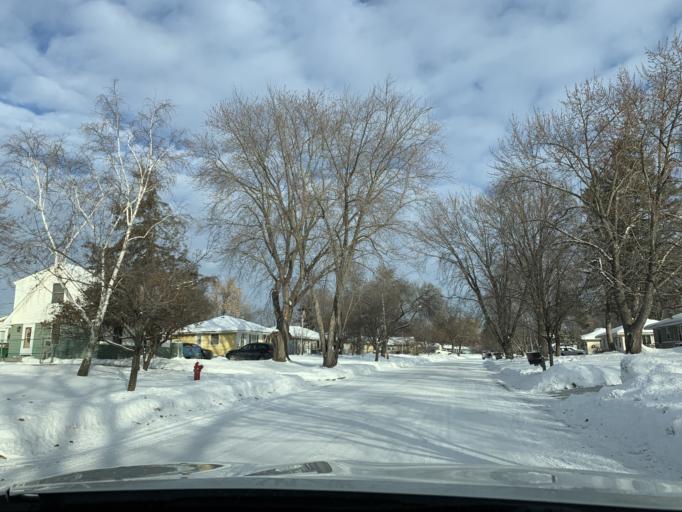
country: US
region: Minnesota
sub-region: Anoka County
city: Coon Rapids
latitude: 45.1761
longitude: -93.2893
